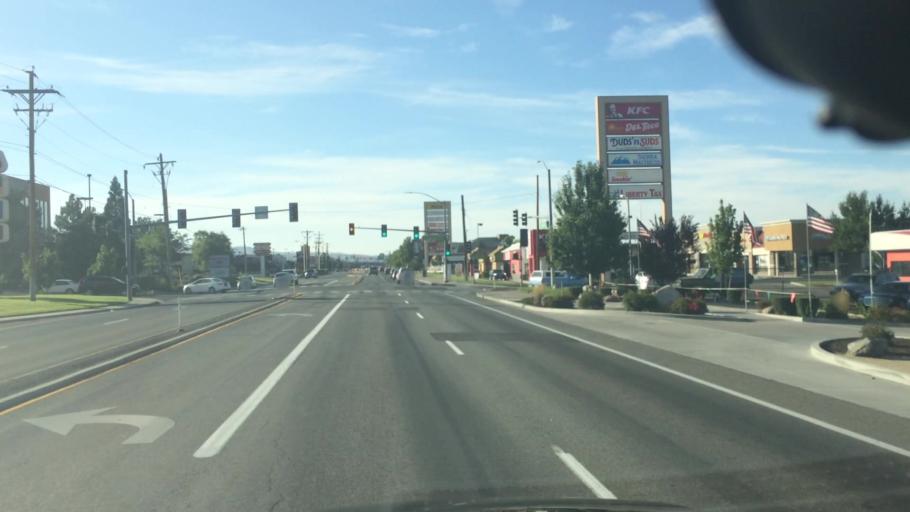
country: US
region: Nevada
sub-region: Washoe County
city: Reno
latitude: 39.4705
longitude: -119.7860
